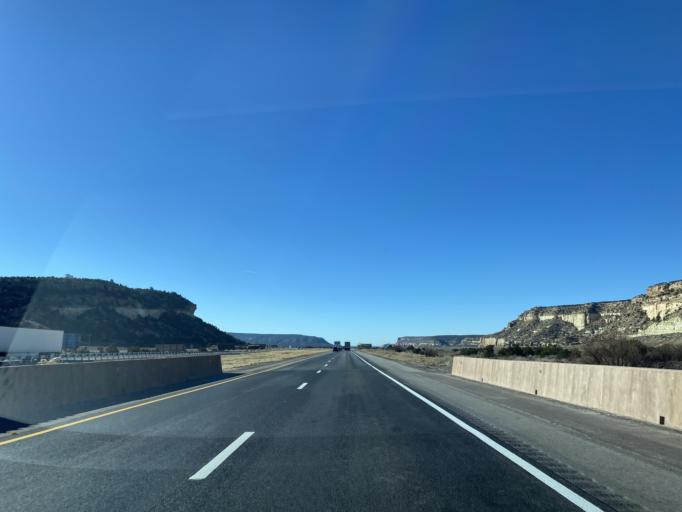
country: US
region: Arizona
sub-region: Apache County
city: Houck
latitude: 35.4149
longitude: -108.9945
